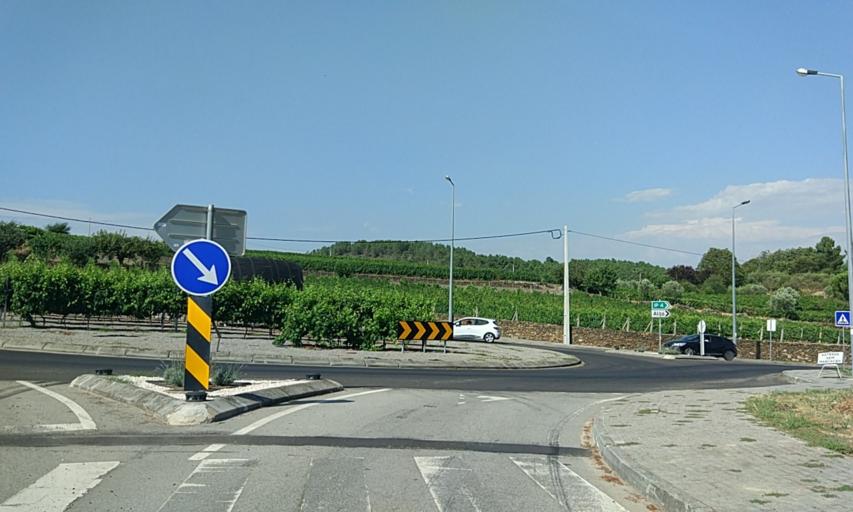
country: PT
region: Vila Real
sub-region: Sabrosa
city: Sabrosa
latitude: 41.2627
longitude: -7.4918
